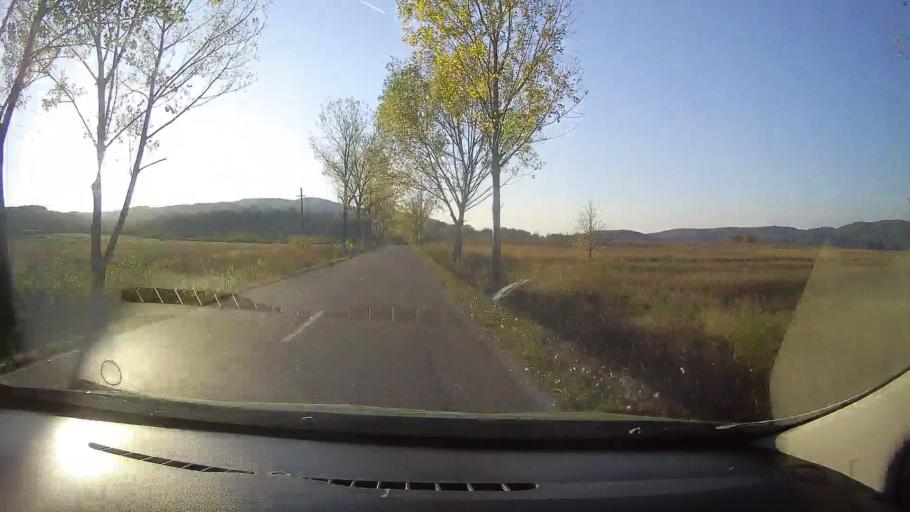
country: RO
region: Timis
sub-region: Comuna Fardea
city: Fardea
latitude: 45.7443
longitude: 22.1461
